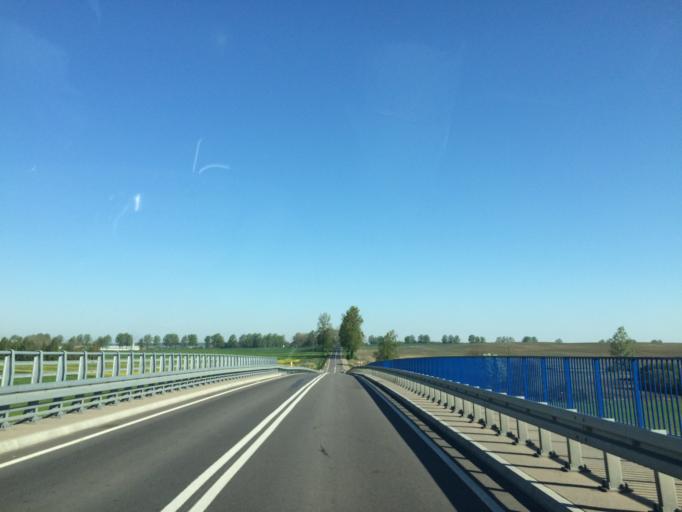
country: PL
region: Warmian-Masurian Voivodeship
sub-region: Powiat ilawski
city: Lubawa
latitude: 53.4103
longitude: 19.7945
